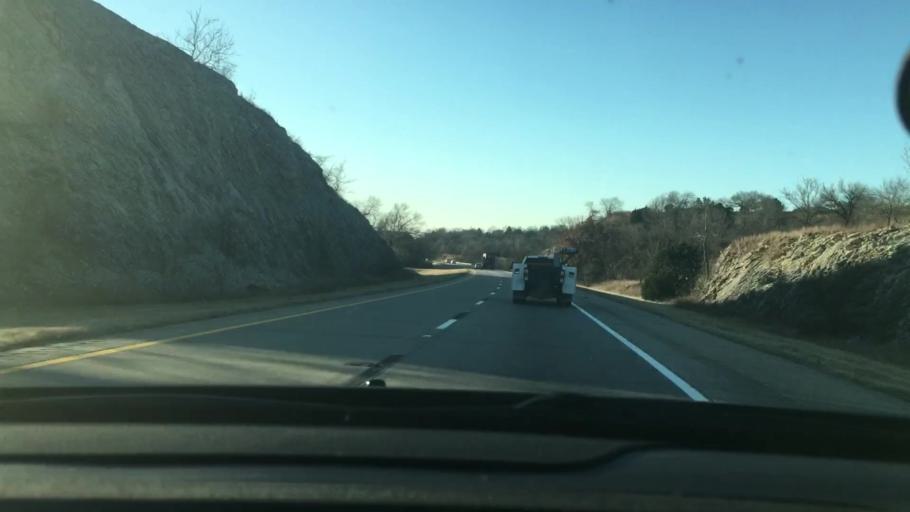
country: US
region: Oklahoma
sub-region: Murray County
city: Davis
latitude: 34.3584
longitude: -97.1490
